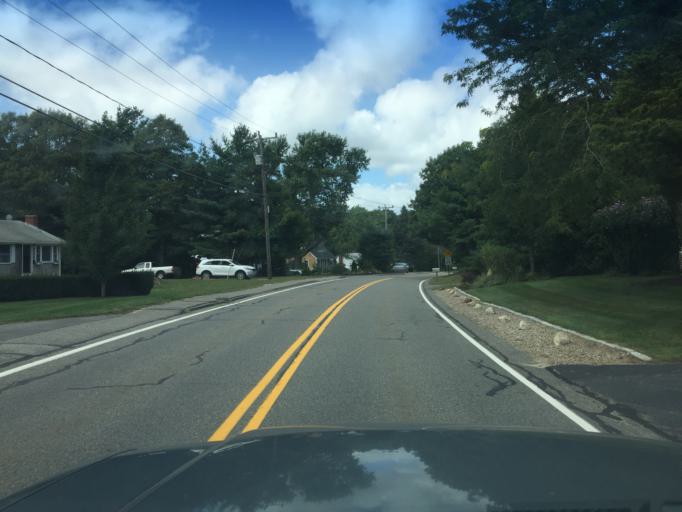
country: US
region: Massachusetts
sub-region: Barnstable County
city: Monument Beach
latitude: 41.7163
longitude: -70.6054
